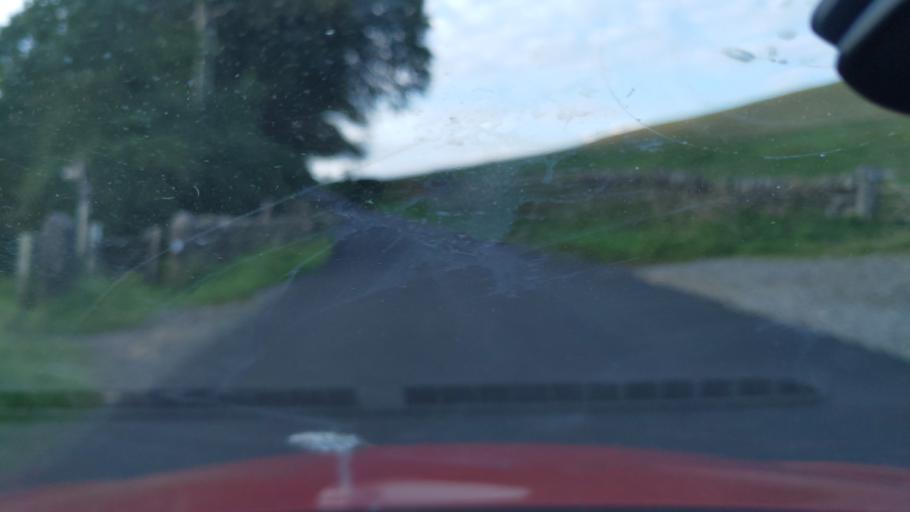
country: GB
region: England
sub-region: Blackburn with Darwen
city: Darwen
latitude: 53.6724
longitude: -2.5073
